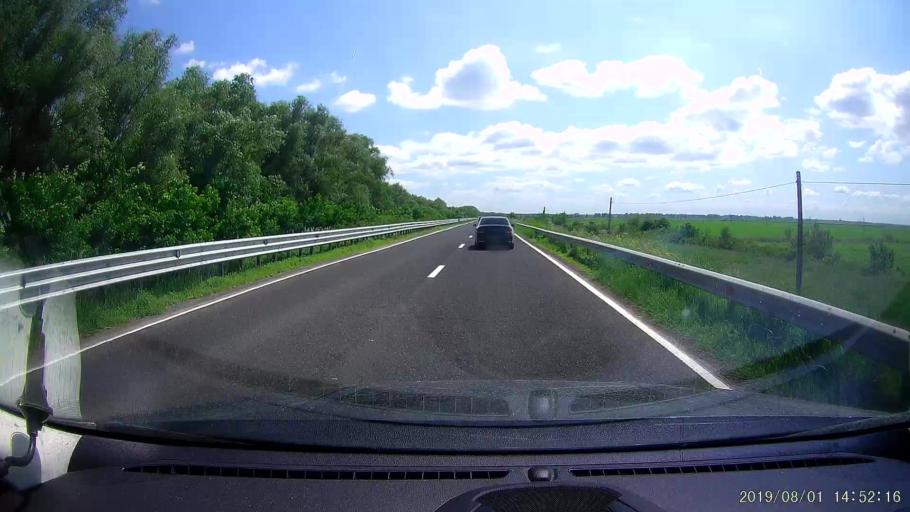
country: RO
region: Braila
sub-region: Comuna Vadeni
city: Vadeni
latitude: 45.3585
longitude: 28.0117
